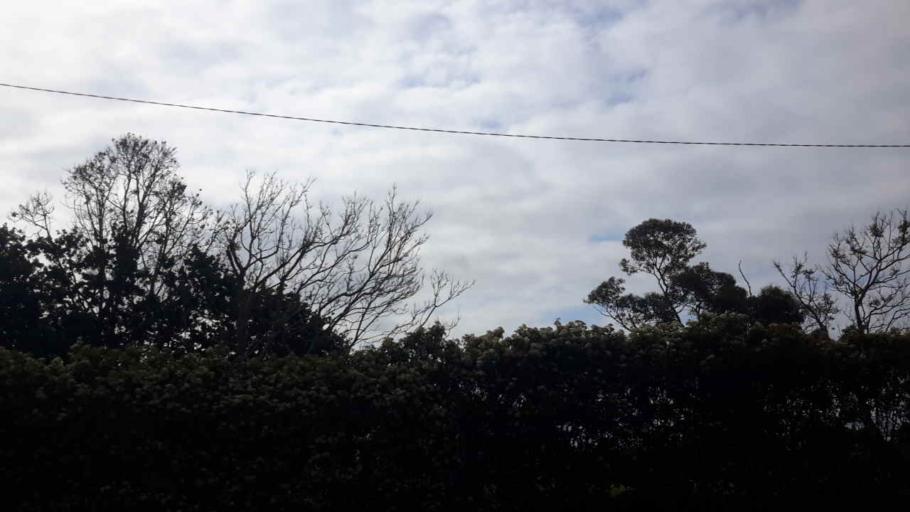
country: AU
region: New South Wales
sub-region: Campbelltown Municipality
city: Glen Alpine
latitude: -34.1091
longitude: 150.7481
